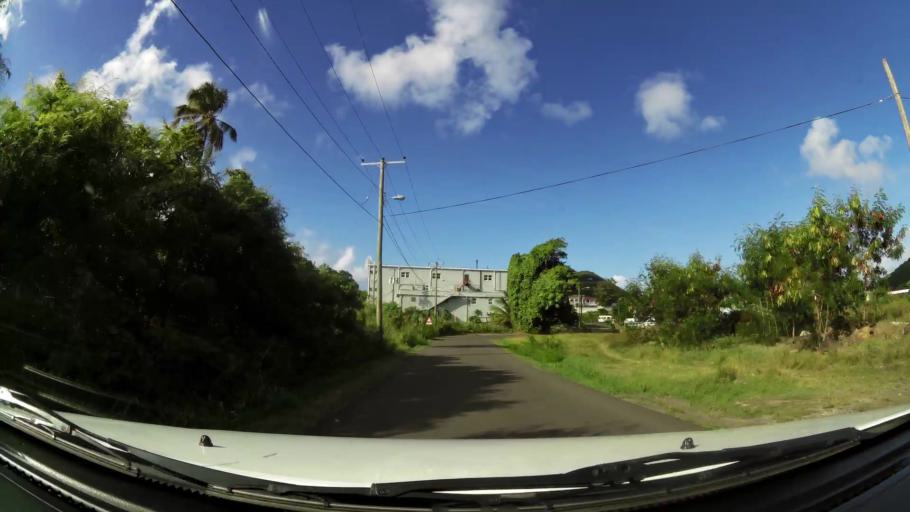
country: LC
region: Gros-Islet
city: Gros Islet
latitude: 14.0531
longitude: -60.9635
